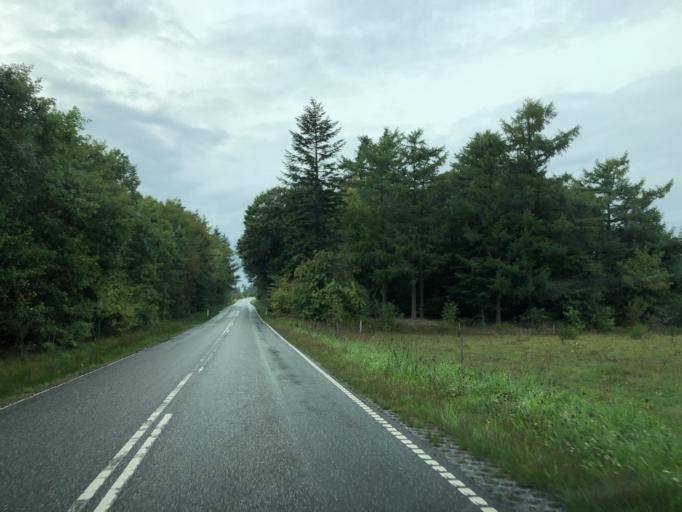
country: DK
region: Central Jutland
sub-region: Ikast-Brande Kommune
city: Brande
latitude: 55.9961
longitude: 9.1980
